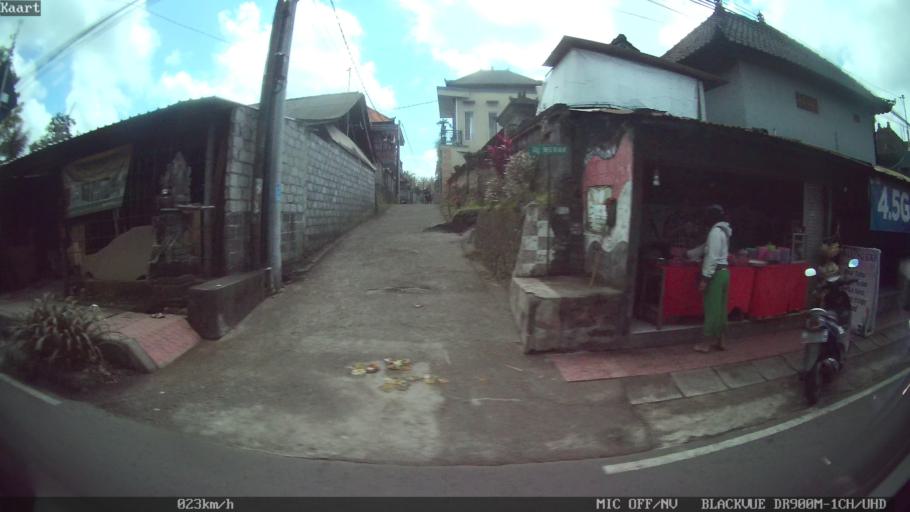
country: ID
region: Bali
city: Banjar Sedang
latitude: -8.5635
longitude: 115.2755
